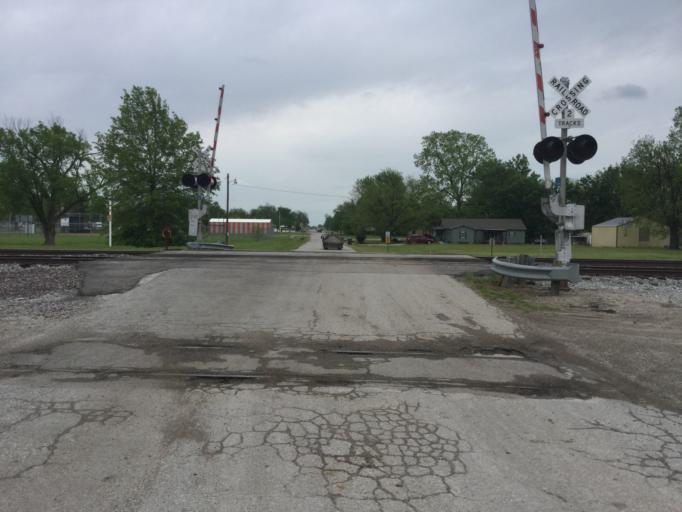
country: US
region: Kansas
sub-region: Labette County
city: Chetopa
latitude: 37.0369
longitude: -95.1022
